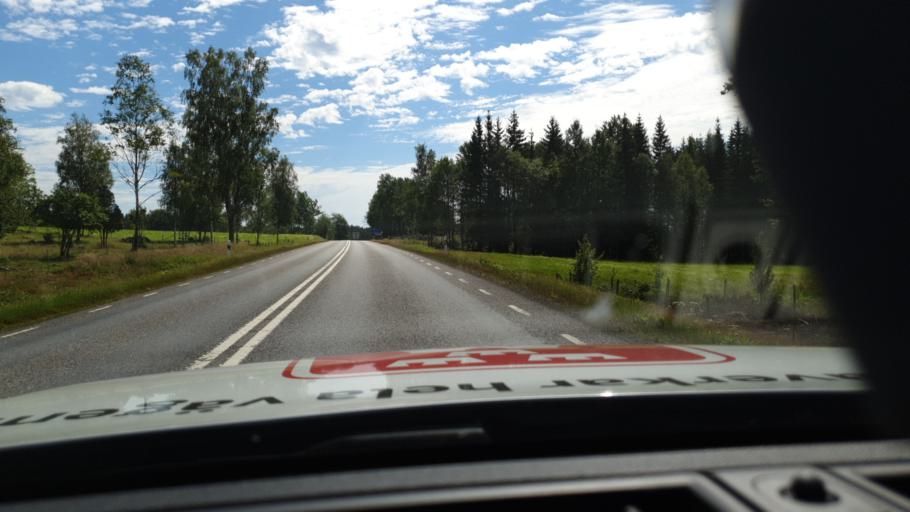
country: SE
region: Kronoberg
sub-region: Vaxjo Kommun
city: Lammhult
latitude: 57.1985
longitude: 14.5261
